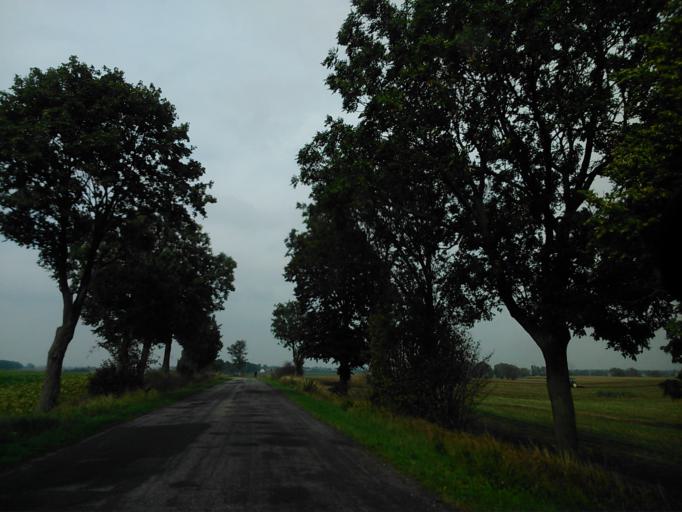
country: PL
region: Kujawsko-Pomorskie
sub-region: Powiat wabrzeski
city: Pluznica
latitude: 53.2398
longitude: 18.8181
